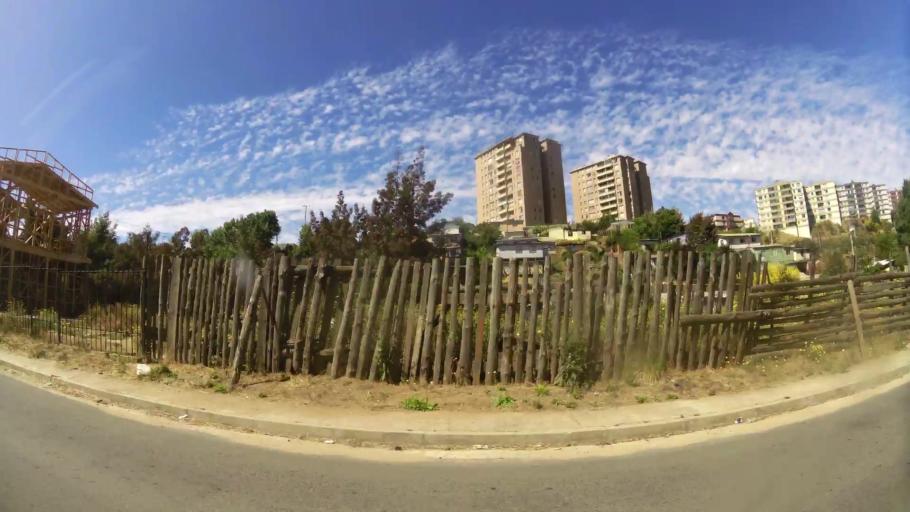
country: CL
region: Valparaiso
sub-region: Provincia de Valparaiso
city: Vina del Mar
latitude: -33.0446
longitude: -71.5757
